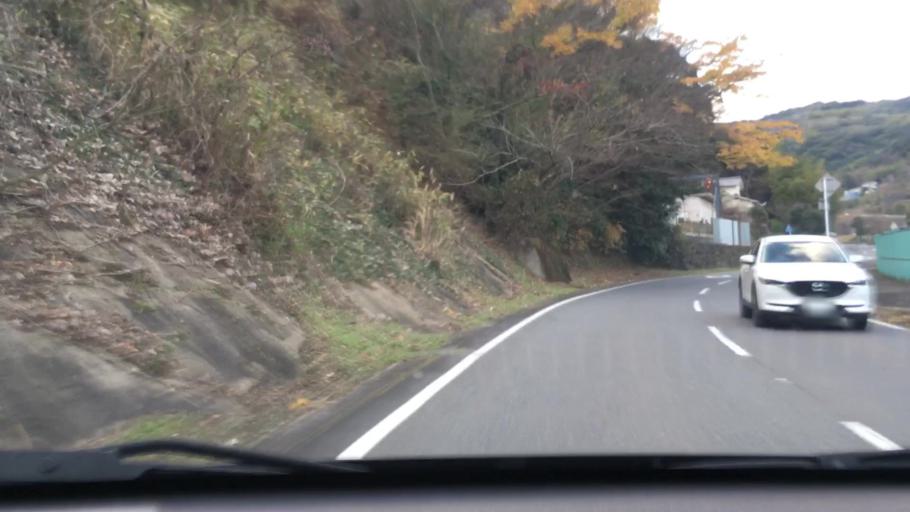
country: JP
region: Oita
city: Hiji
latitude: 33.3604
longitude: 131.4923
